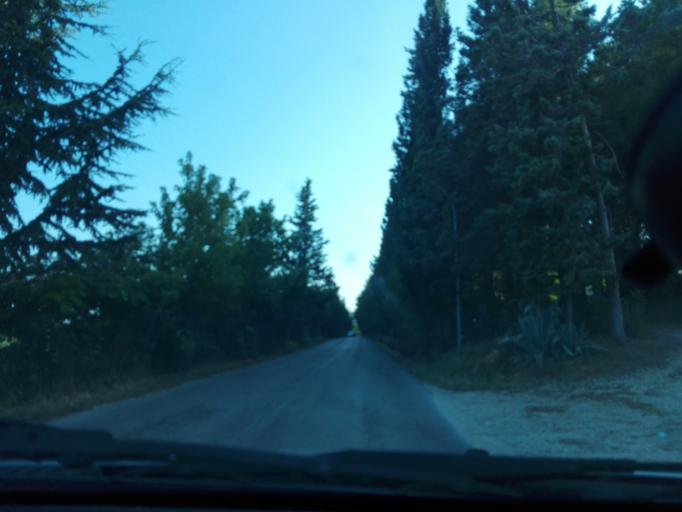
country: IT
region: Abruzzo
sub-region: Provincia di Pescara
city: Cappelle sul Tavo
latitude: 42.4551
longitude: 14.0925
